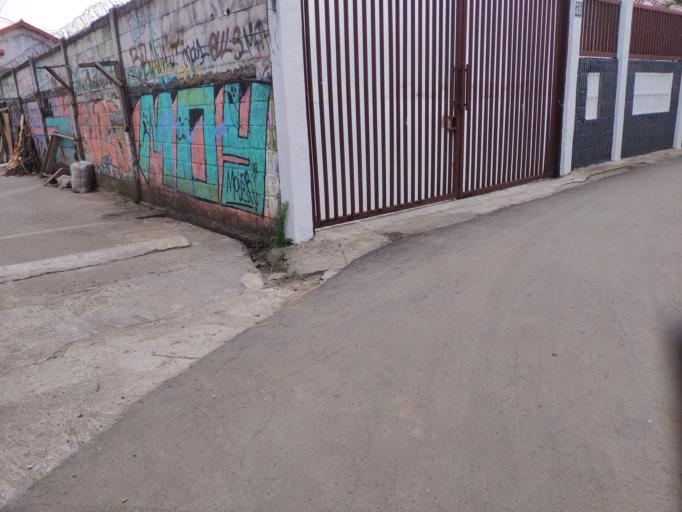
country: ID
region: West Java
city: Pamulang
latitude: -6.3239
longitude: 106.7992
